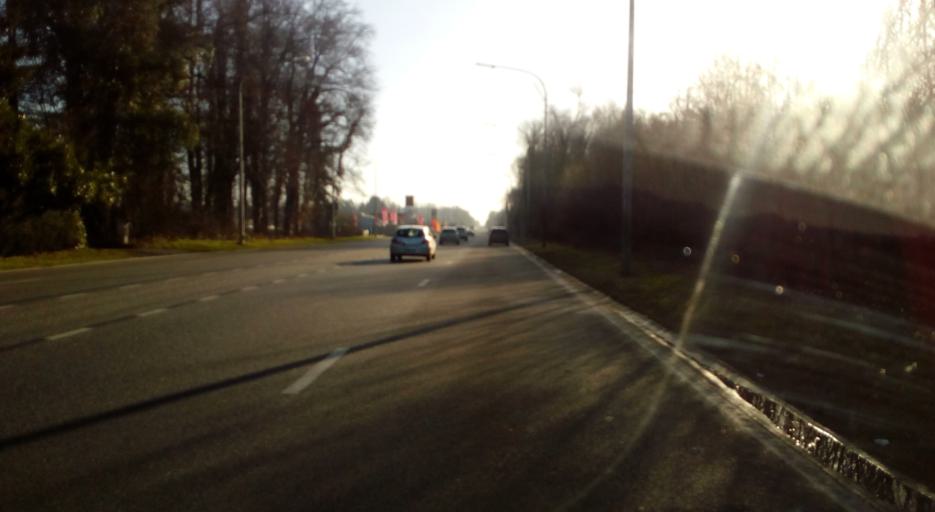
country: BE
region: Wallonia
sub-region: Province du Hainaut
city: Gerpinnes
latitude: 50.3331
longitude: 4.4752
